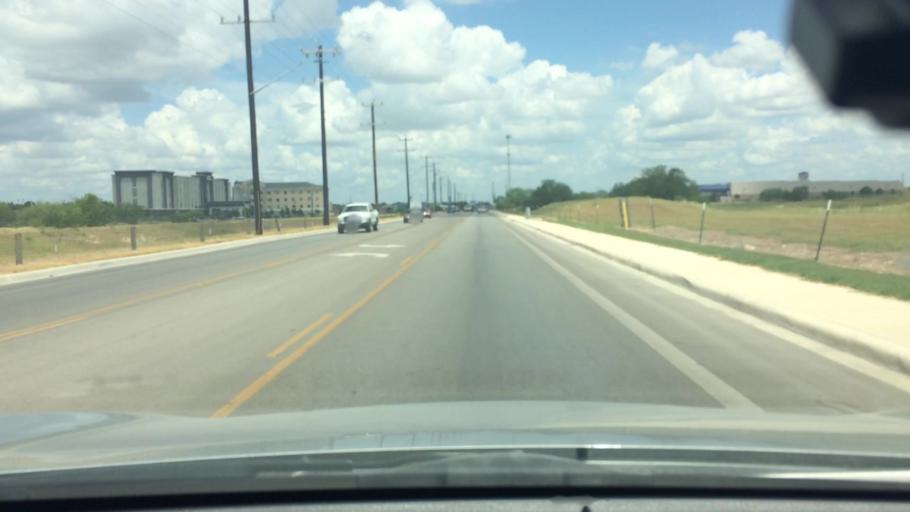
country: US
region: Texas
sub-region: Bexar County
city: China Grove
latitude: 29.3443
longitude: -98.4263
